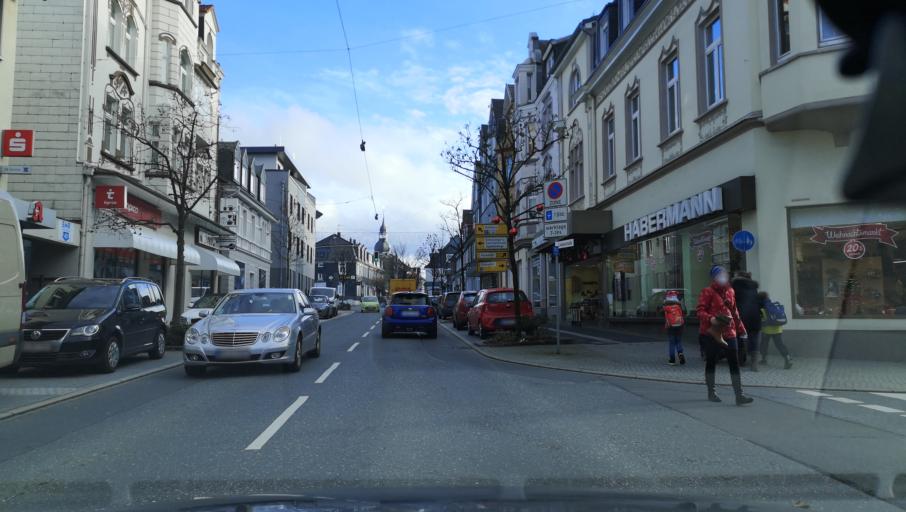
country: DE
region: North Rhine-Westphalia
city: Radevormwald
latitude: 51.2033
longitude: 7.3535
